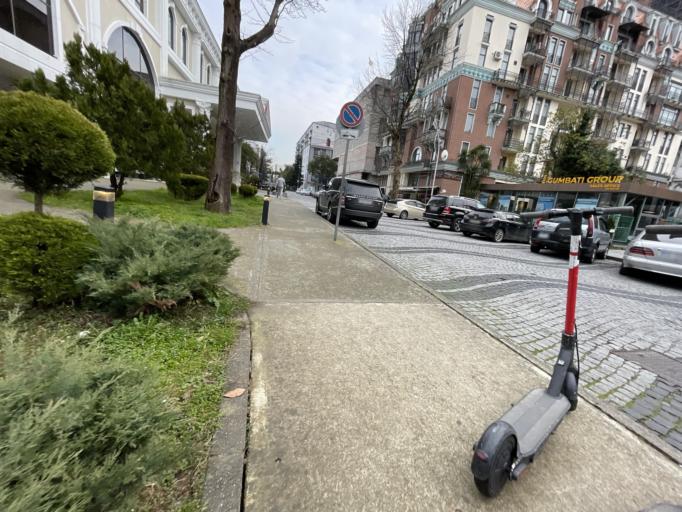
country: GE
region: Ajaria
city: Batumi
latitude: 41.6510
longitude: 41.6295
